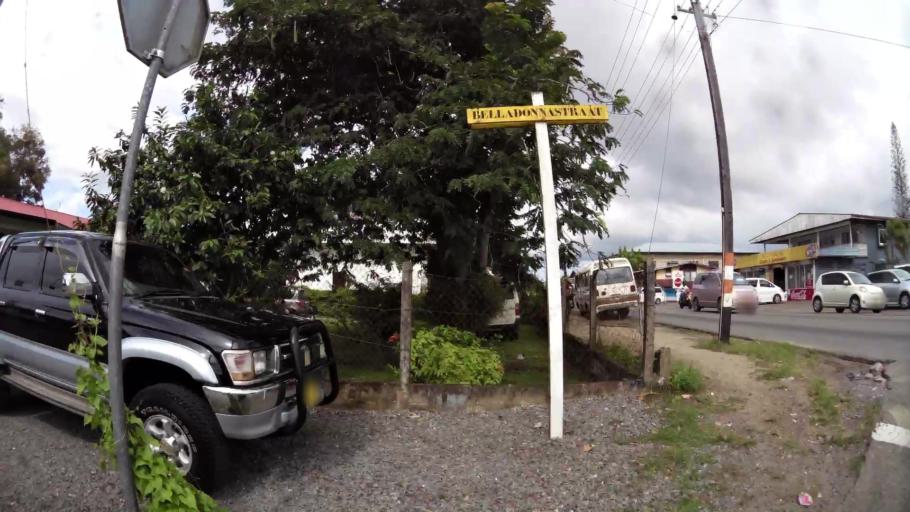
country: SR
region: Paramaribo
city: Paramaribo
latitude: 5.8419
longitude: -55.1930
